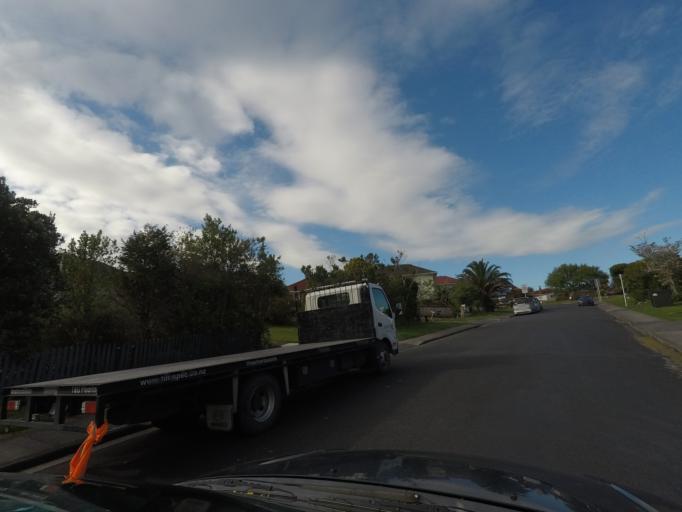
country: NZ
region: Auckland
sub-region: Auckland
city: Rosebank
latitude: -36.8708
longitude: 174.6442
